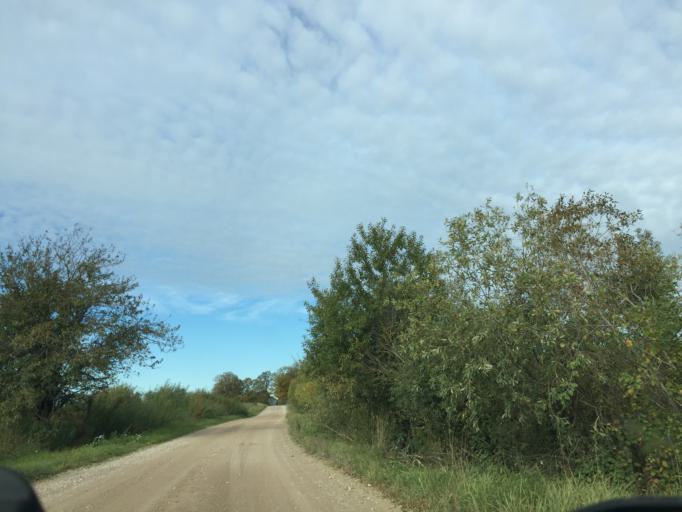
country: LV
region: Jaunpils
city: Jaunpils
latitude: 56.6203
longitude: 23.0654
